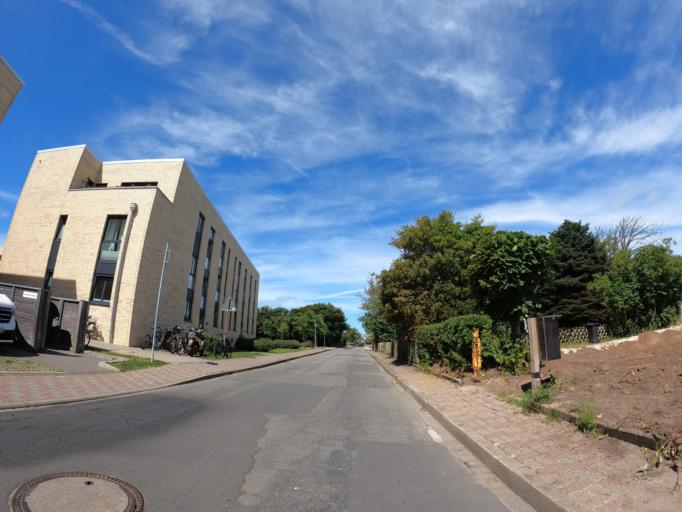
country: DE
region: Schleswig-Holstein
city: Westerland
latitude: 54.9114
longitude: 8.3171
